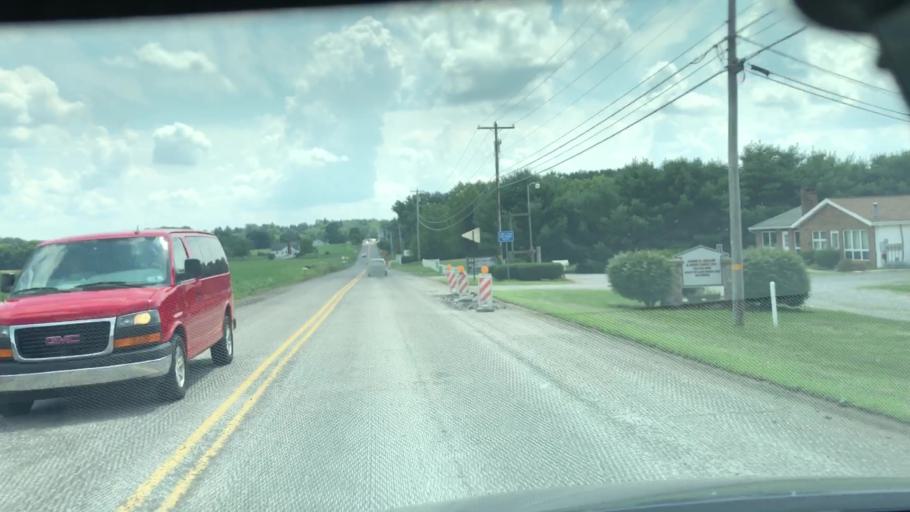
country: US
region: Pennsylvania
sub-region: Butler County
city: Saxonburg
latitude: 40.7809
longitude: -79.7975
